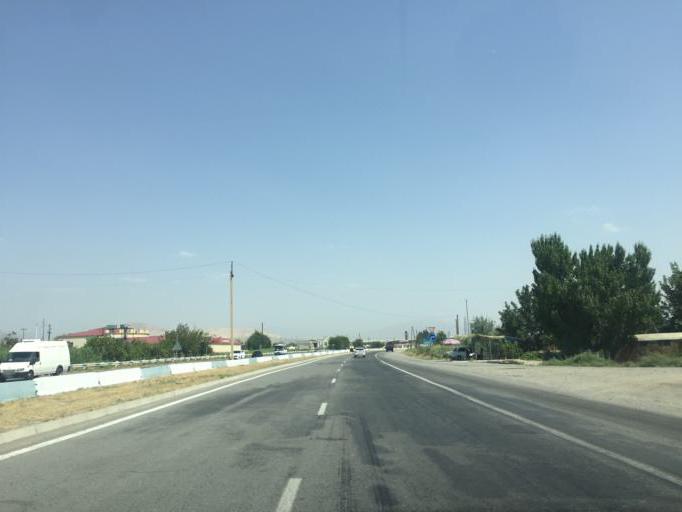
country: AM
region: Ararat
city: Artashat
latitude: 39.9569
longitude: 44.5309
